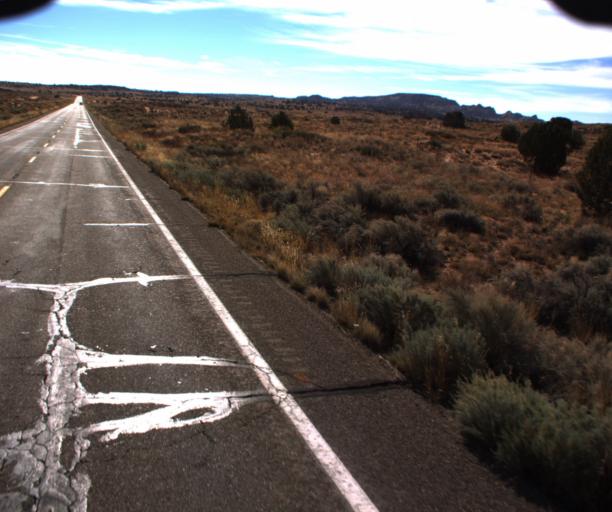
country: US
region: Arizona
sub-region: Coconino County
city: Kaibito
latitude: 36.5913
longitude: -111.1582
